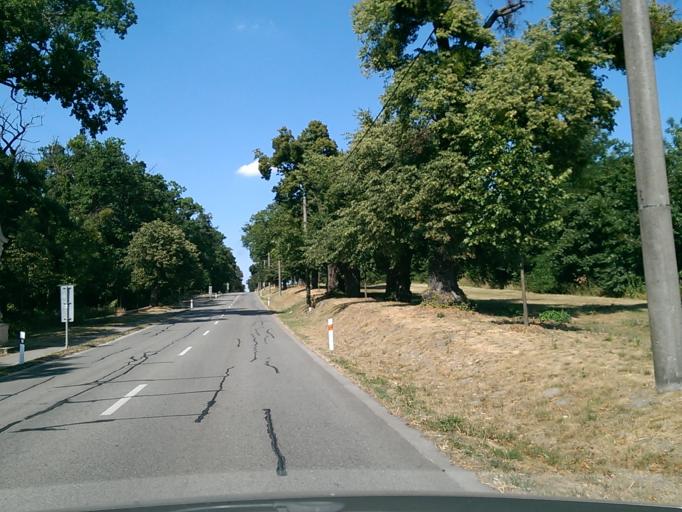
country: CZ
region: South Moravian
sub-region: Okres Breclav
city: Valtice
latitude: 48.7493
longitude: 16.7632
